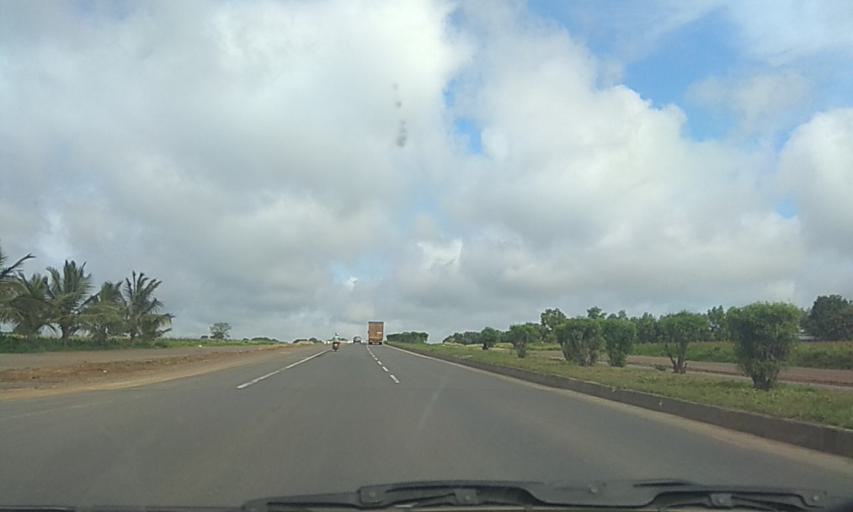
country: IN
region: Karnataka
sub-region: Haveri
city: Shiggaon
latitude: 15.0059
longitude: 75.2021
